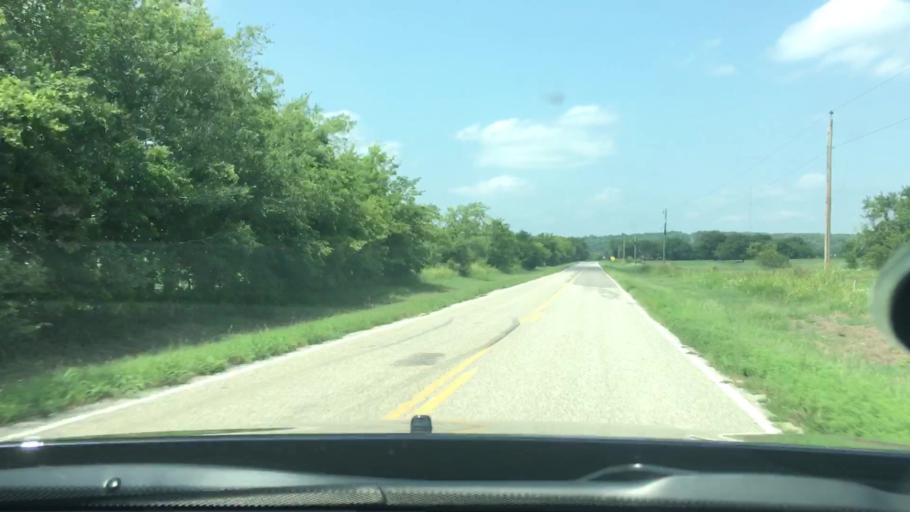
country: US
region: Oklahoma
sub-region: Johnston County
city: Tishomingo
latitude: 34.4071
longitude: -96.4965
